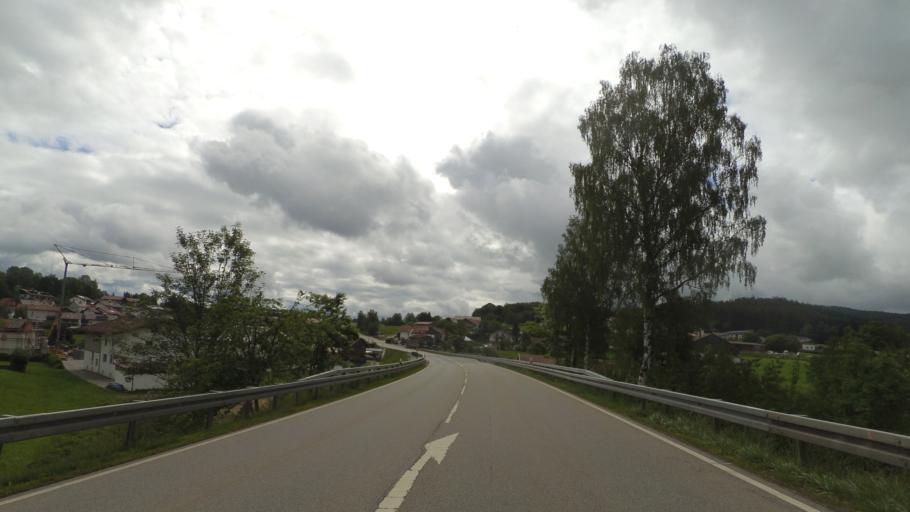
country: DE
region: Bavaria
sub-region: Lower Bavaria
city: Prackenbach
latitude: 49.0927
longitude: 12.8241
